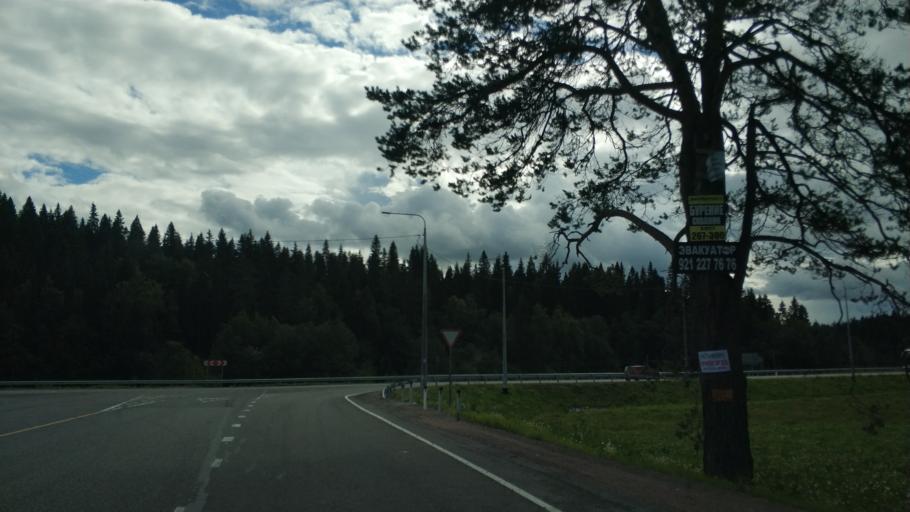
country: RU
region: Republic of Karelia
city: Khelyulya
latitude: 61.7762
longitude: 30.6615
